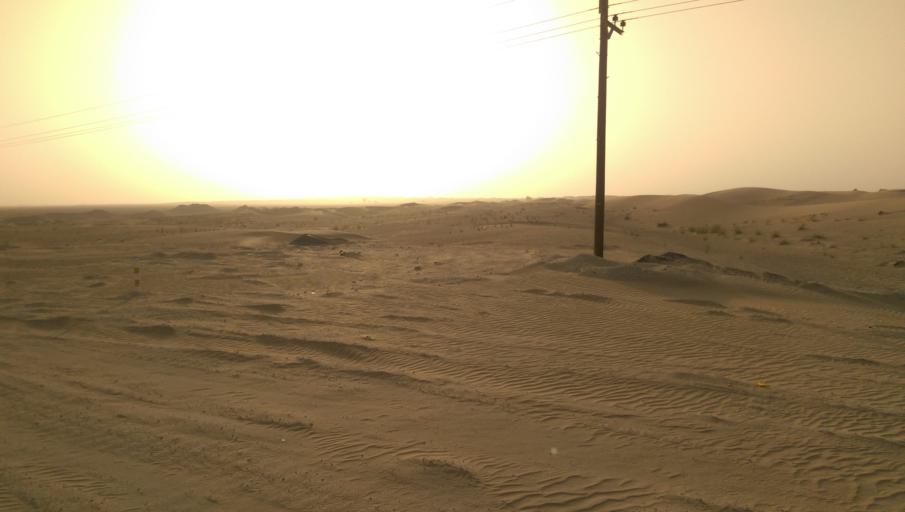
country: AE
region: Dubai
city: Dubai
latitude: 24.7911
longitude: 55.3745
